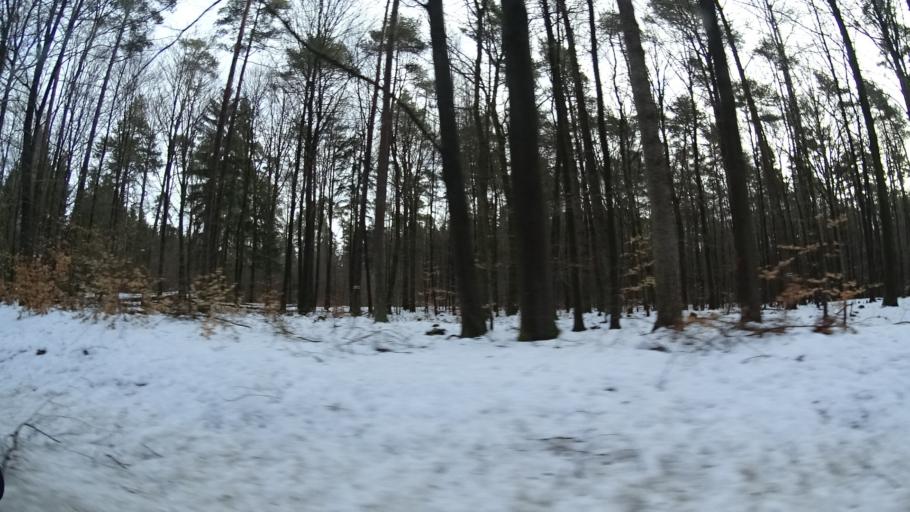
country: DE
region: Baden-Wuerttemberg
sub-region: Karlsruhe Region
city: Fahrenbach
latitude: 49.4908
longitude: 9.1456
